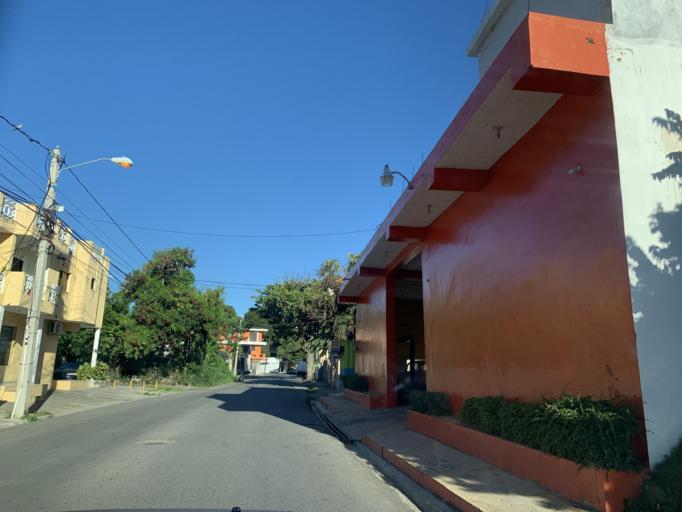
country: DO
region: Puerto Plata
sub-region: Puerto Plata
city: Puerto Plata
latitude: 19.7898
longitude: -70.6957
